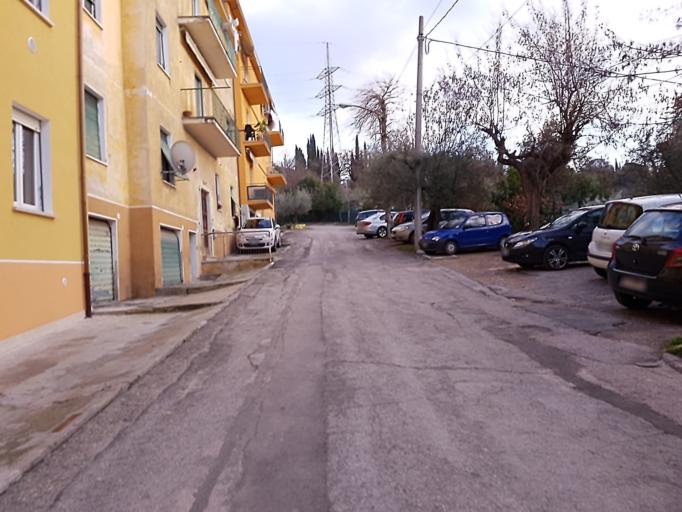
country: IT
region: Umbria
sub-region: Provincia di Perugia
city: Perugia
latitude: 43.0995
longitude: 12.3776
